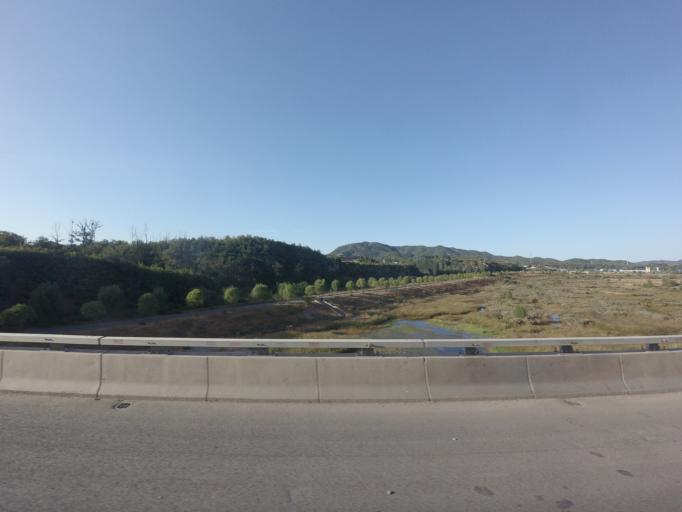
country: CN
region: Beijing
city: Jugezhuang
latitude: 40.3916
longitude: 116.9053
